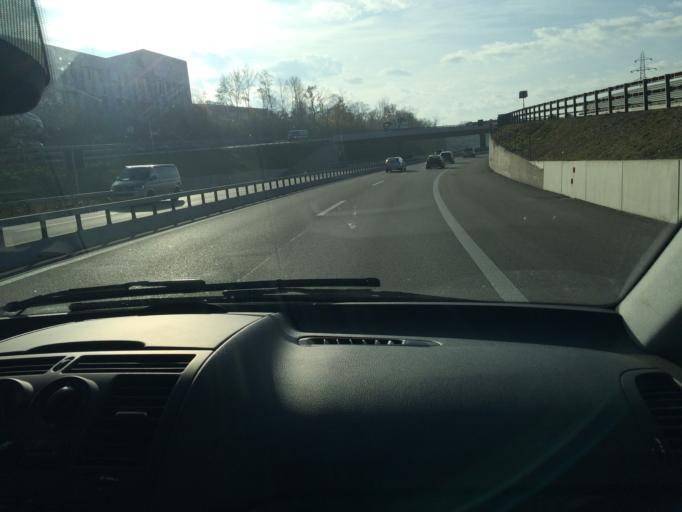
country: CH
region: Bern
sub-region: Bern-Mittelland District
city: Bolligen
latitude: 46.9730
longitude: 7.4709
